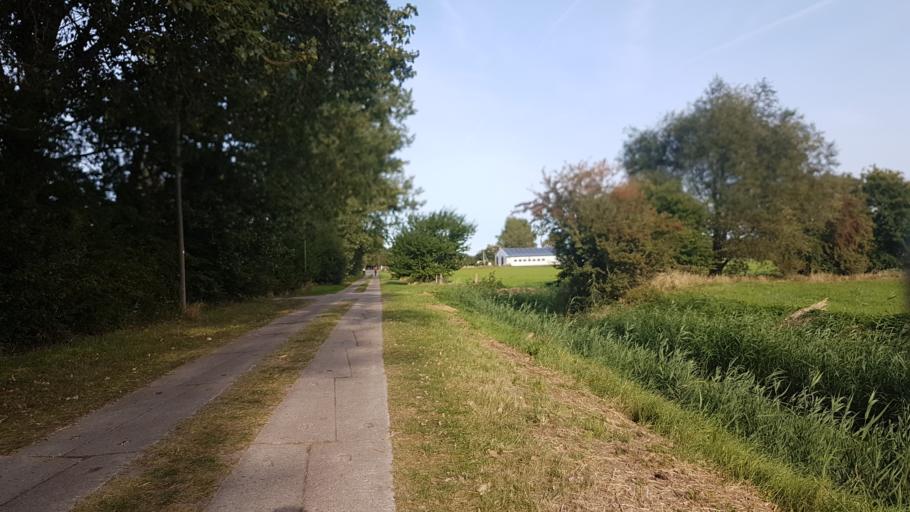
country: DE
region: Mecklenburg-Vorpommern
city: Rambin
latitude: 54.4507
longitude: 13.1419
